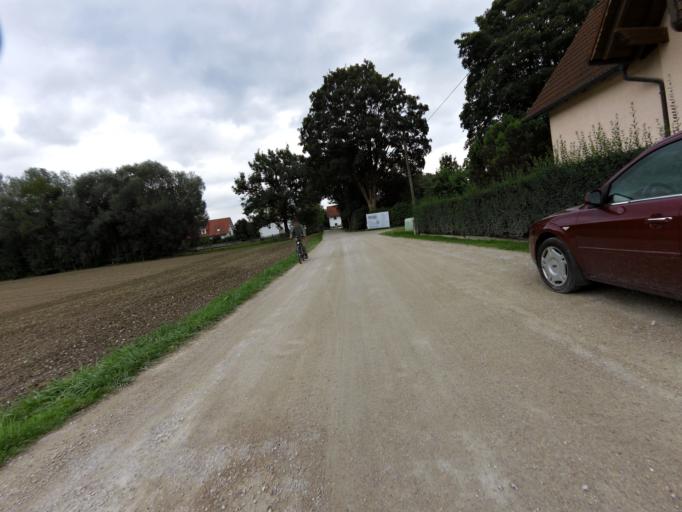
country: DE
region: Bavaria
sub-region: Lower Bavaria
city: Tiefenbach
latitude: 48.5361
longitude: 12.1132
